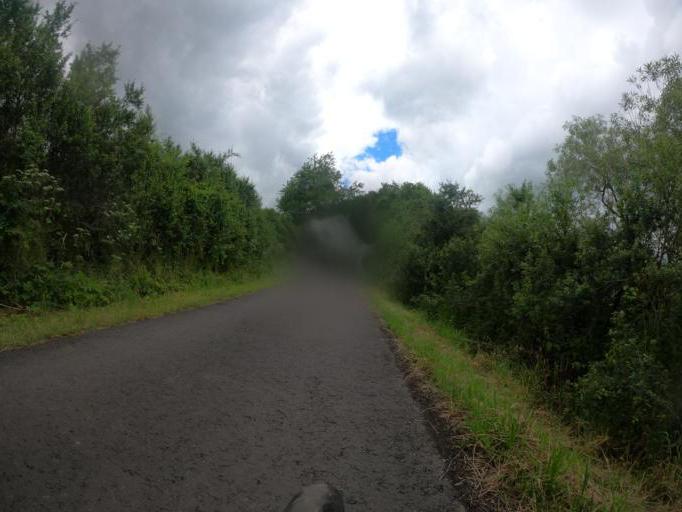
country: DE
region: Hesse
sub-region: Regierungsbezirk Kassel
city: Grossalmerode
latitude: 51.1890
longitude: 9.7901
